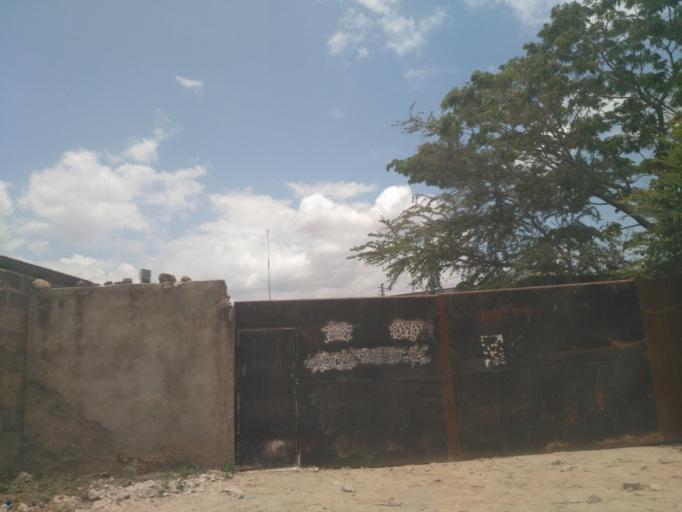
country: TZ
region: Dar es Salaam
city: Dar es Salaam
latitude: -6.8561
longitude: 39.2873
